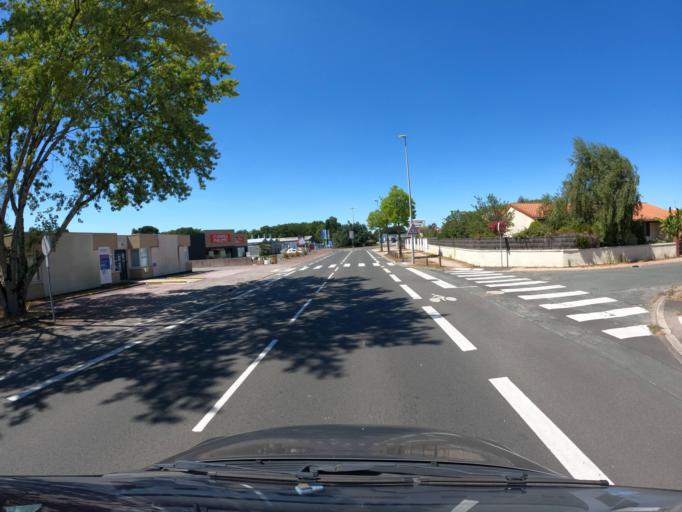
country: FR
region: Pays de la Loire
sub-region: Departement de la Vendee
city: Challans
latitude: 46.8379
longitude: -1.8844
